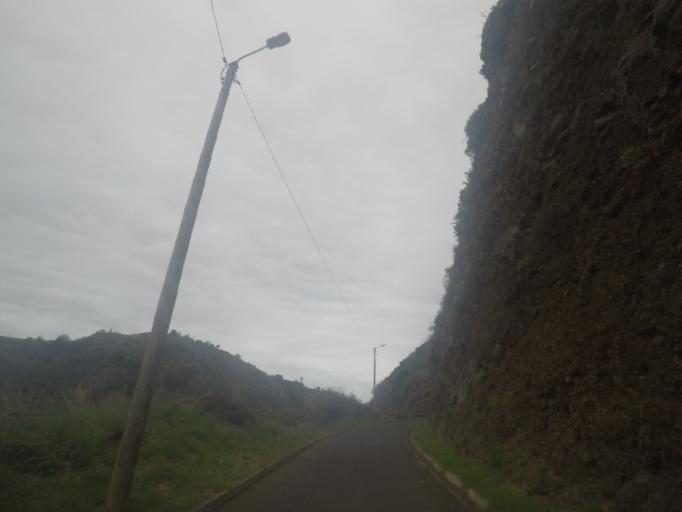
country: PT
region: Madeira
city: Camara de Lobos
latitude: 32.6644
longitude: -16.9617
